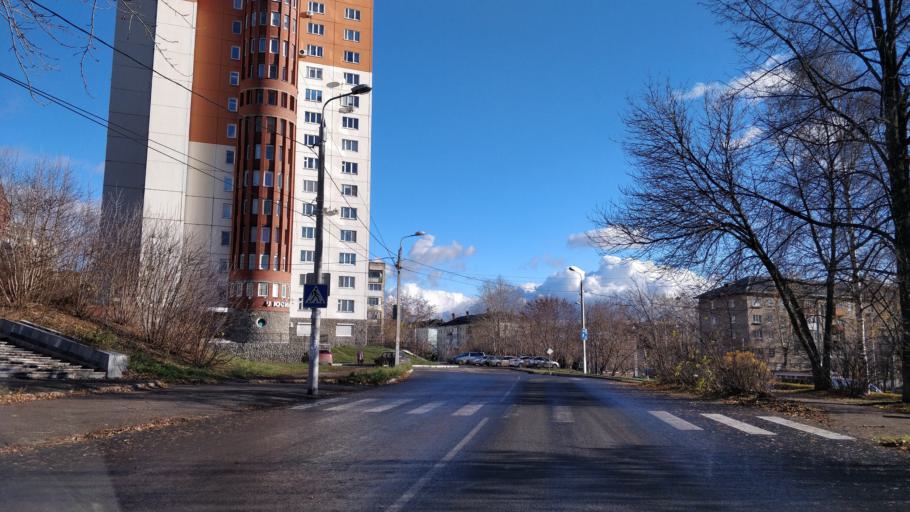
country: RU
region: Perm
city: Perm
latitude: 58.0068
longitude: 56.1991
